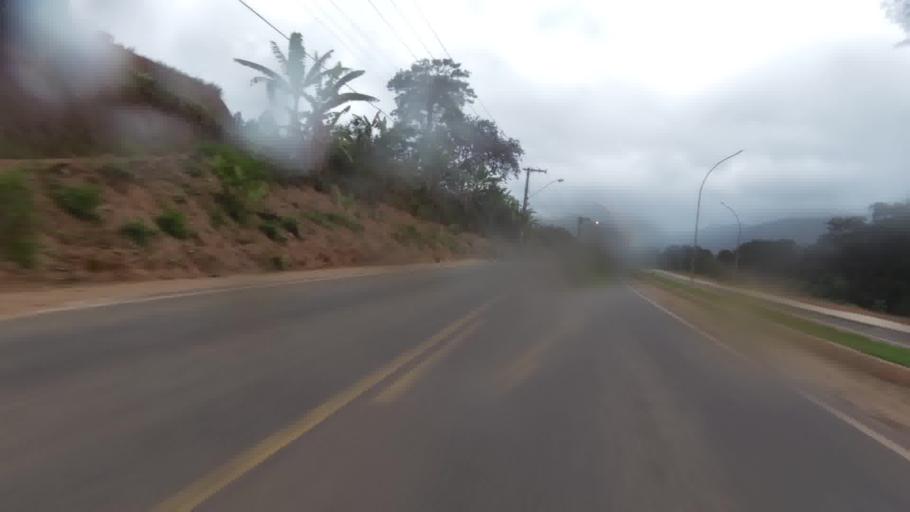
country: BR
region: Espirito Santo
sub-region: Alfredo Chaves
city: Alfredo Chaves
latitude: -20.6454
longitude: -40.7471
